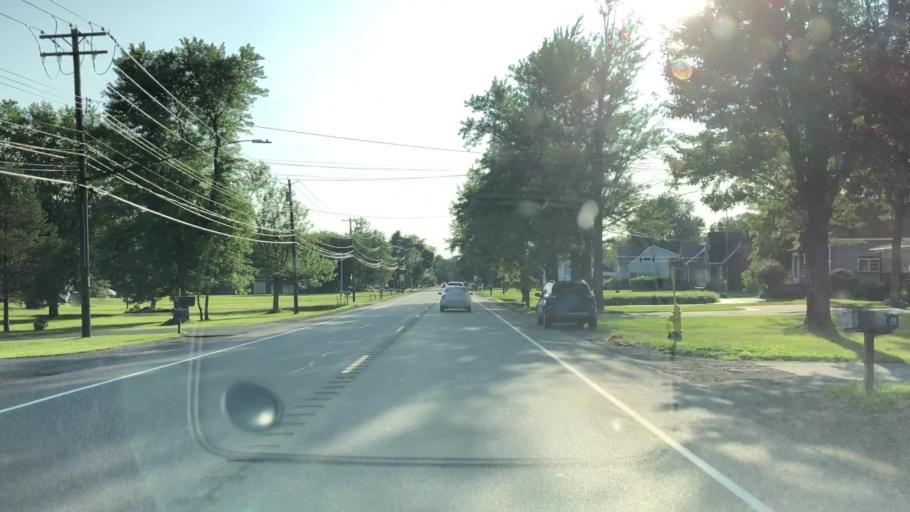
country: US
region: New York
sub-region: Erie County
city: Cheektowaga
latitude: 42.8563
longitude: -78.7437
